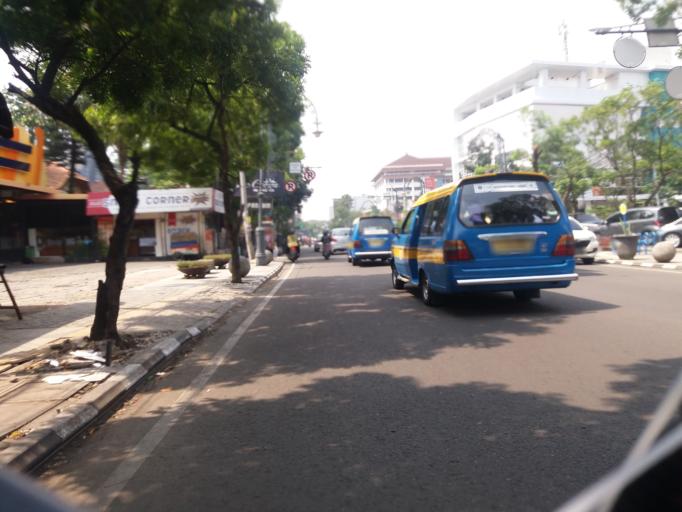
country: ID
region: West Java
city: Bandung
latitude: -6.9064
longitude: 107.6150
